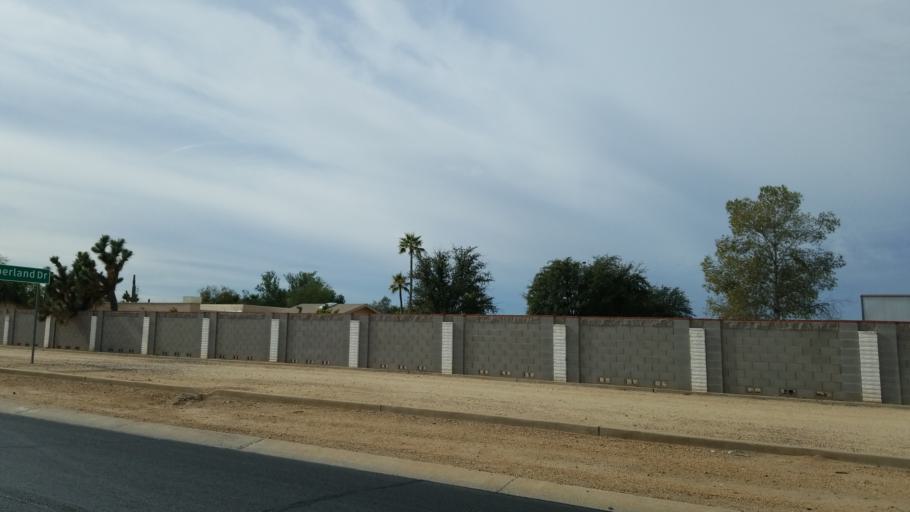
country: US
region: Arizona
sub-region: Maricopa County
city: Youngtown
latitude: 33.5760
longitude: -112.2988
